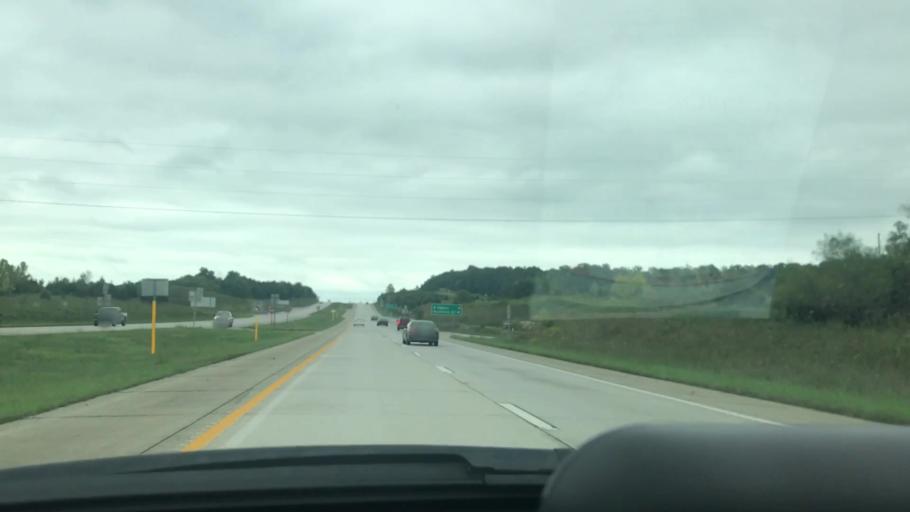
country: US
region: Missouri
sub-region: Greene County
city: Fair Grove
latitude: 37.5149
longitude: -93.1385
